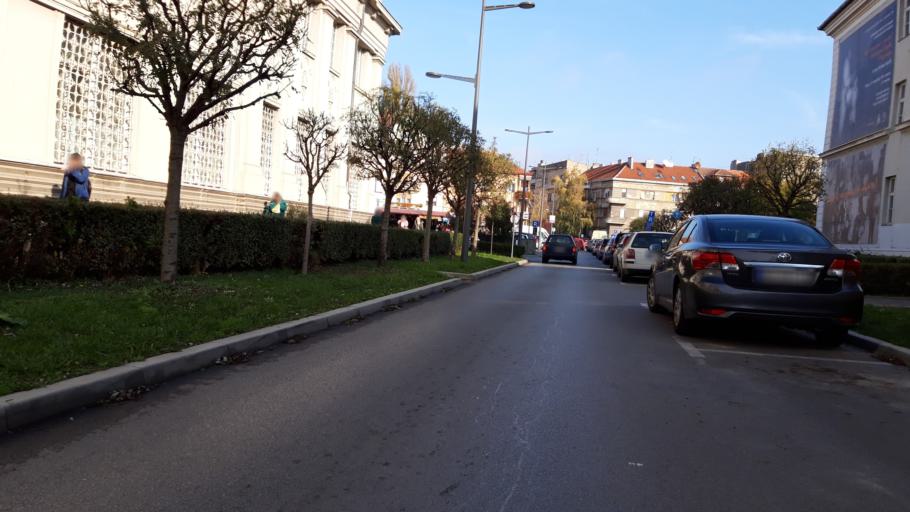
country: RS
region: Autonomna Pokrajina Vojvodina
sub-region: Juznobacki Okrug
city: Novi Sad
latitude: 45.2567
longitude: 19.8512
